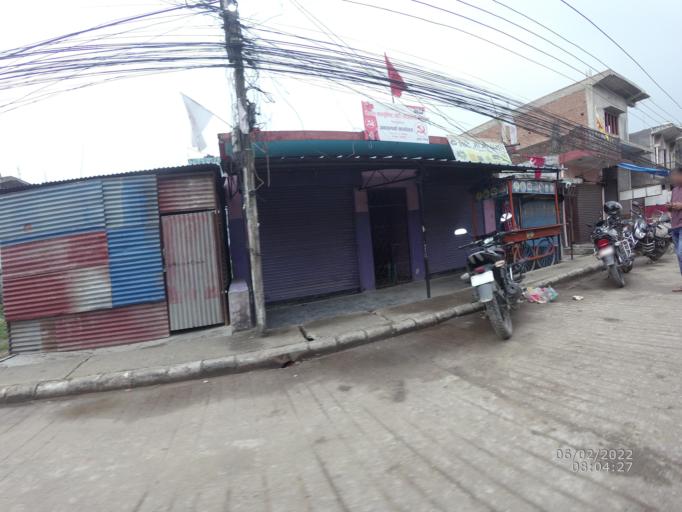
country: NP
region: Western Region
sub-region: Lumbini Zone
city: Bhairahawa
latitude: 27.4766
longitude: 83.4713
